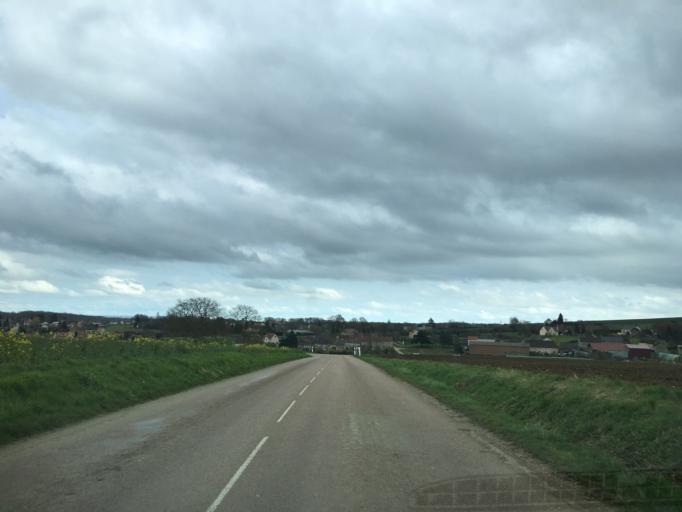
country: FR
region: Bourgogne
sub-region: Departement de l'Yonne
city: Pourrain
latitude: 47.8001
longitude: 3.4258
